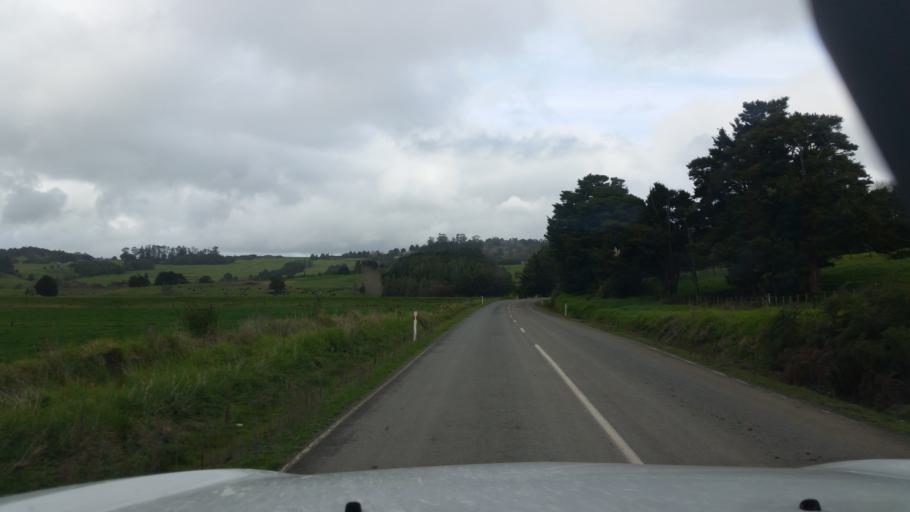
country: NZ
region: Northland
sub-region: Whangarei
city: Maungatapere
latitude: -35.6301
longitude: 174.1971
